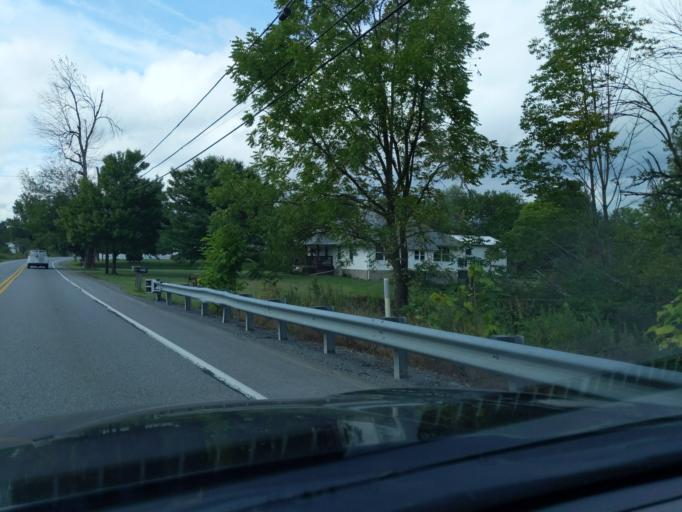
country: US
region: Pennsylvania
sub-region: Blair County
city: Duncansville
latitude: 40.3768
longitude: -78.4201
